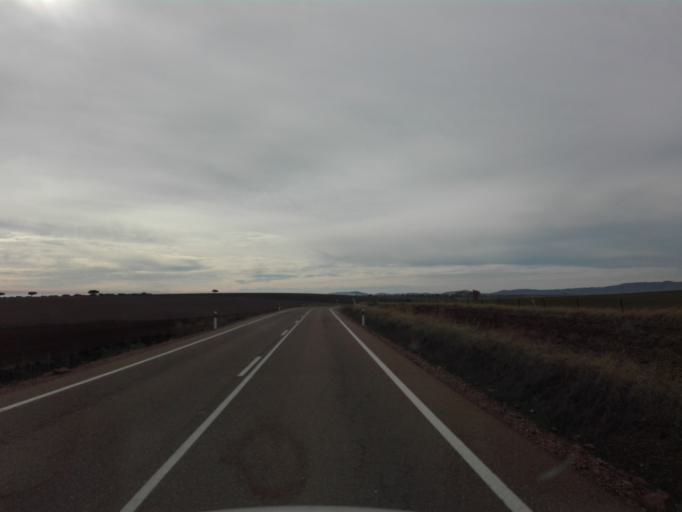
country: ES
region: Extremadura
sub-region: Provincia de Badajoz
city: Valencia de las Torres
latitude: 38.3425
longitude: -5.9647
